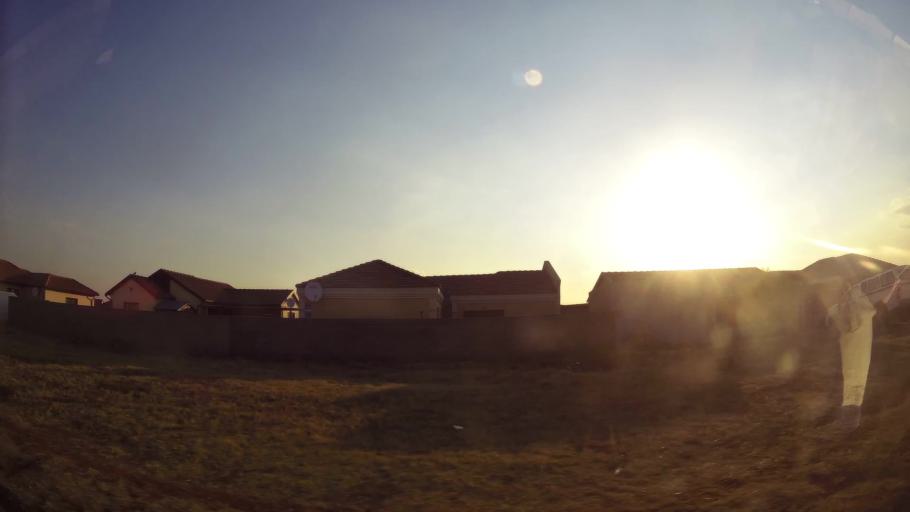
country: ZA
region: Gauteng
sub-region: Ekurhuleni Metropolitan Municipality
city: Boksburg
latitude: -26.2993
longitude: 28.2484
